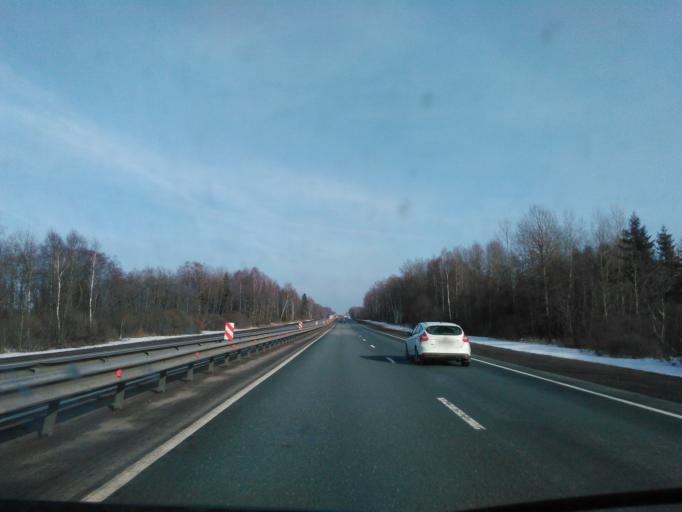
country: RU
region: Smolensk
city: Kholm-Zhirkovskiy
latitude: 55.1862
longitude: 33.7256
